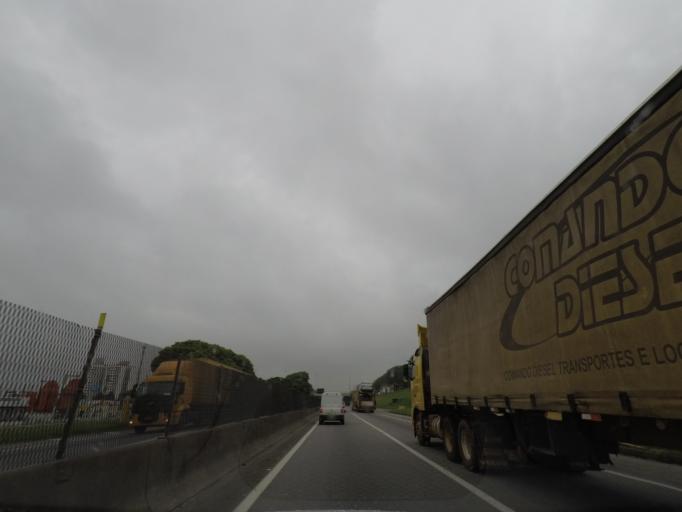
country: BR
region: Sao Paulo
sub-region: Taubate
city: Taubate
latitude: -23.0440
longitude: -45.5804
